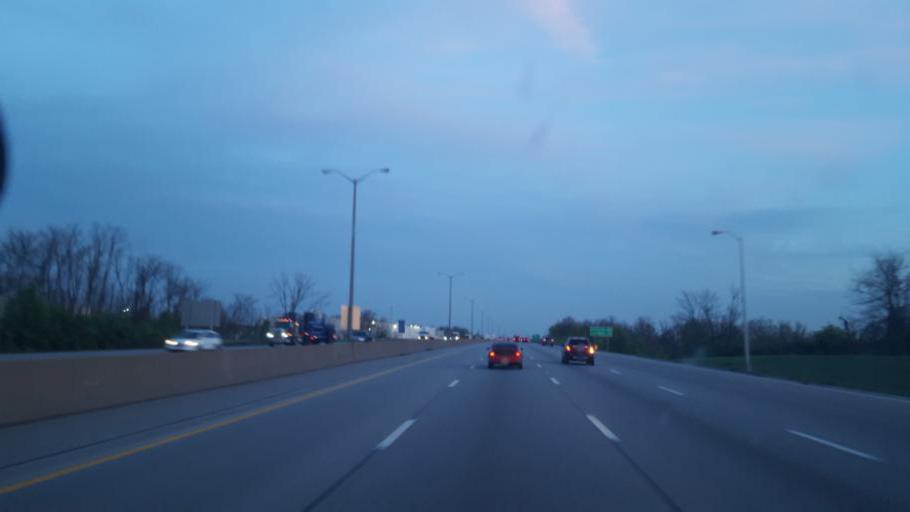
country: US
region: Kentucky
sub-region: Boone County
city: Florence
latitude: 38.9789
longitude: -84.6395
